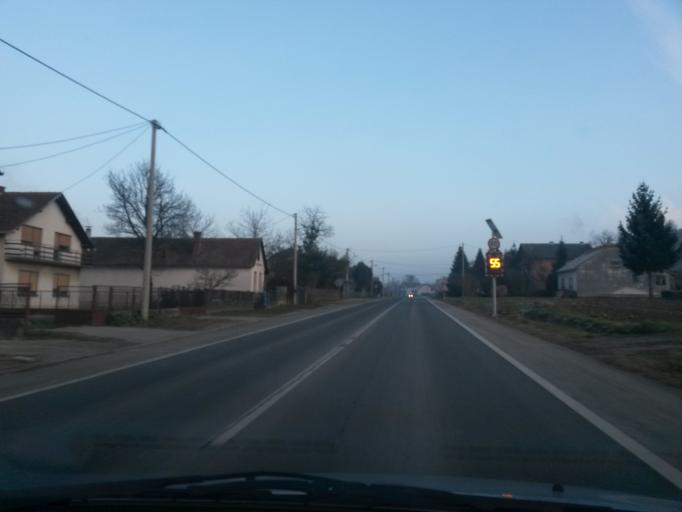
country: HR
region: Varazdinska
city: Ludbreg
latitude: 46.2383
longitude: 16.6370
